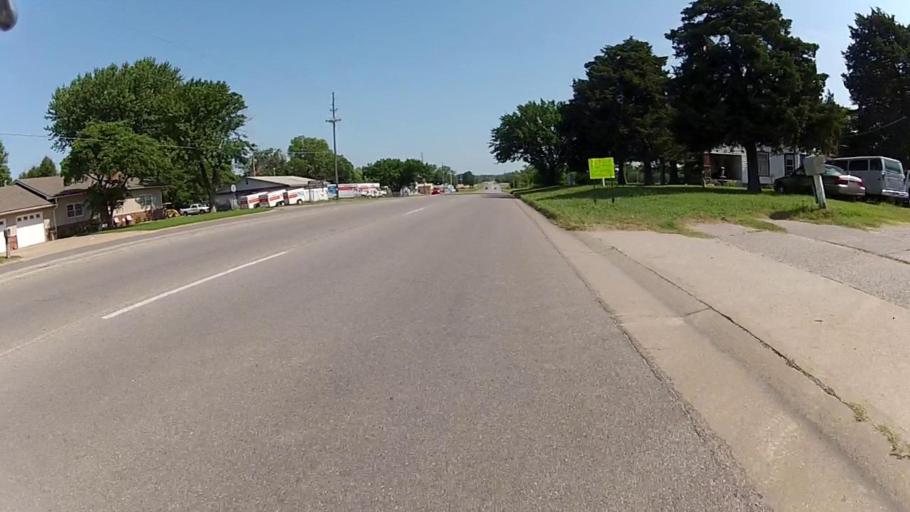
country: US
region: Kansas
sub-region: Montgomery County
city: Independence
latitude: 37.2042
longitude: -95.7106
